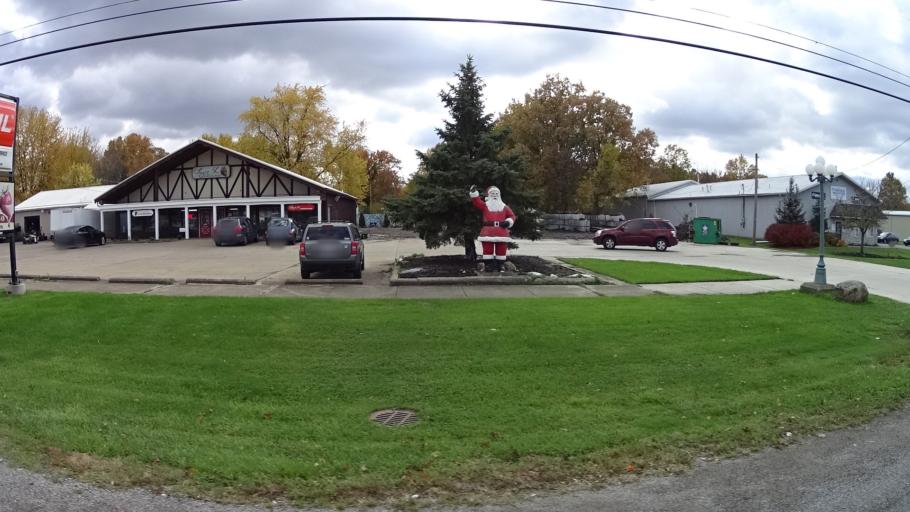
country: US
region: Ohio
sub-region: Lorain County
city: Amherst
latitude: 41.4182
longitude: -82.1939
